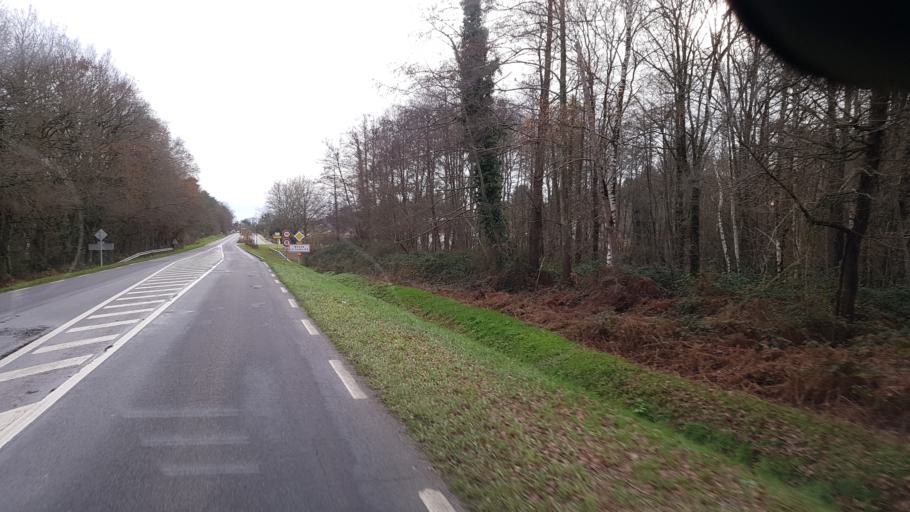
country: FR
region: Centre
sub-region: Departement du Loir-et-Cher
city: Nouan-le-Fuzelier
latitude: 47.5486
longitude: 2.0351
